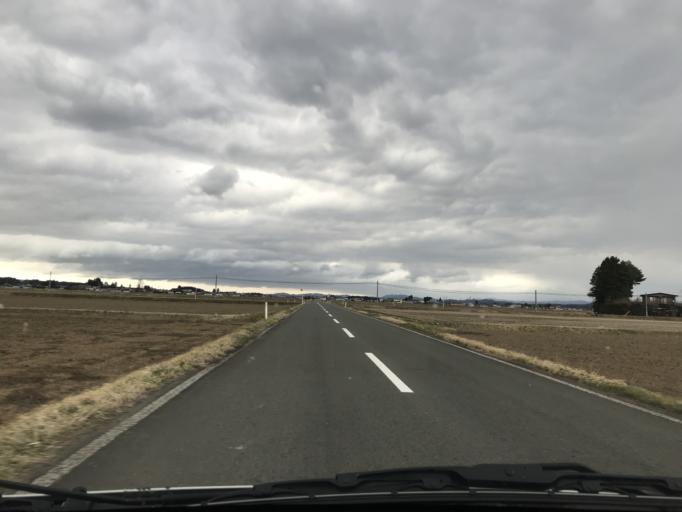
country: JP
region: Iwate
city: Mizusawa
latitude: 39.0919
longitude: 141.1629
